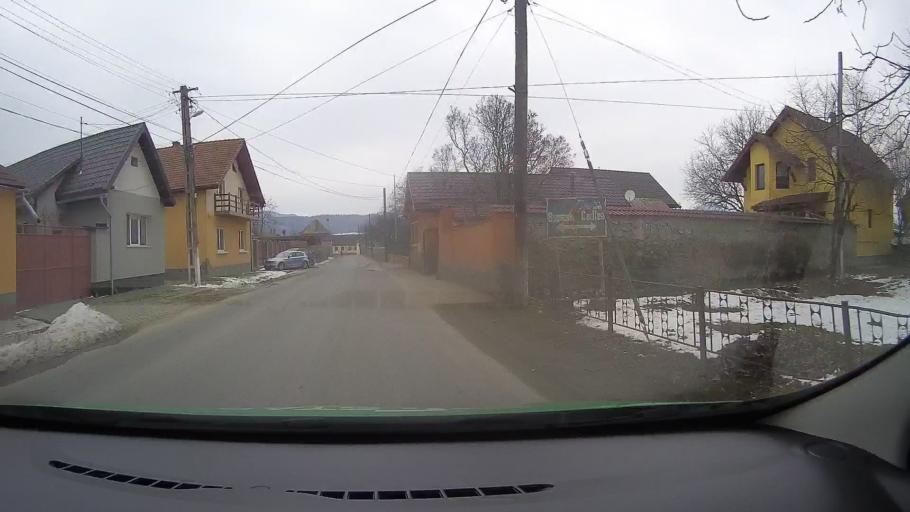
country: RO
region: Brasov
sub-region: Comuna Vulcan
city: Vulcan
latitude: 45.6346
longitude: 25.4253
